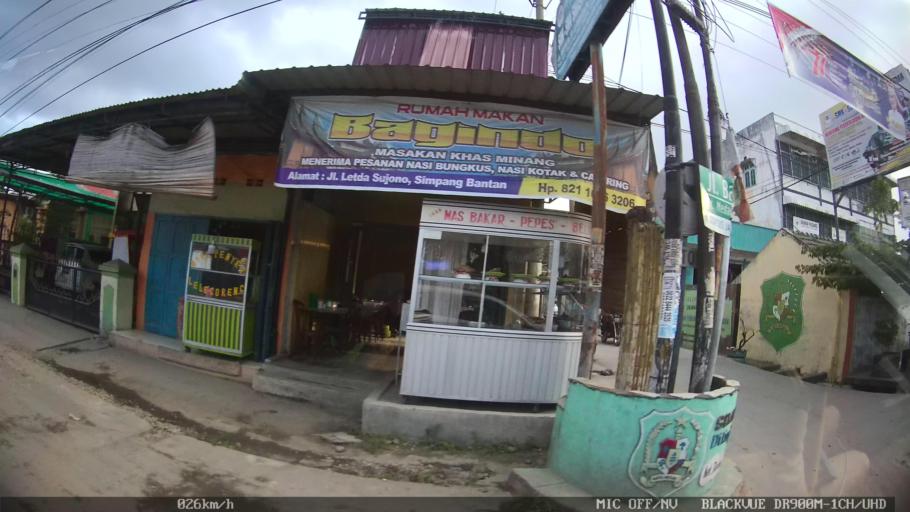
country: ID
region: North Sumatra
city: Medan
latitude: 3.5969
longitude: 98.7357
